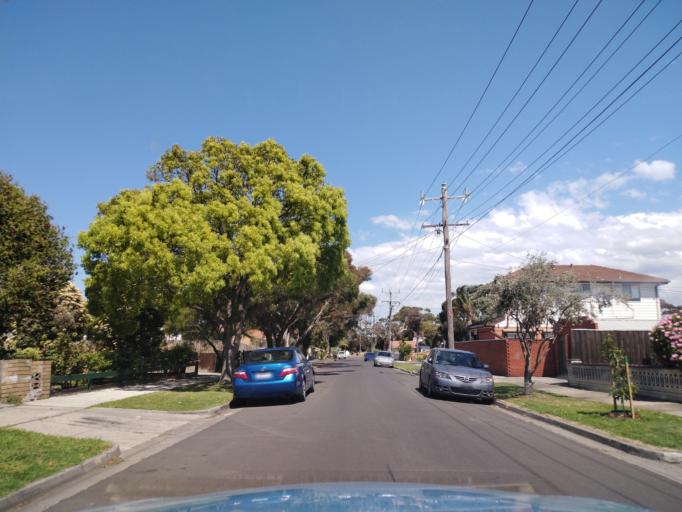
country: AU
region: Victoria
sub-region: Hobsons Bay
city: Altona North
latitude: -37.8381
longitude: 144.8575
